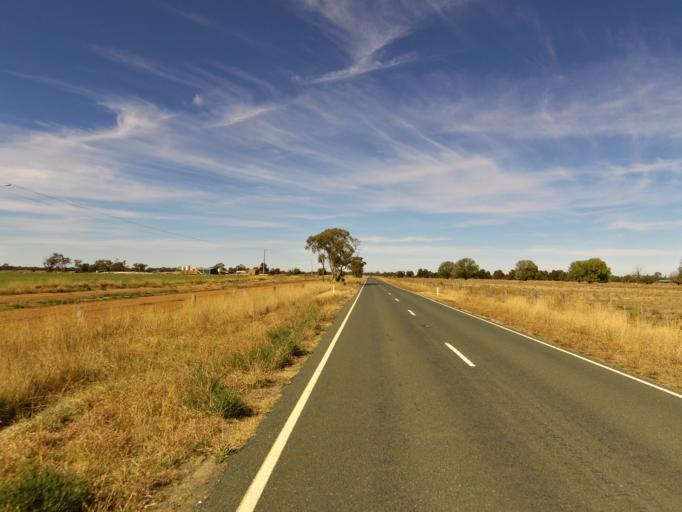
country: AU
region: Victoria
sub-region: Campaspe
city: Echuca
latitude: -36.2916
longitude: 144.5358
